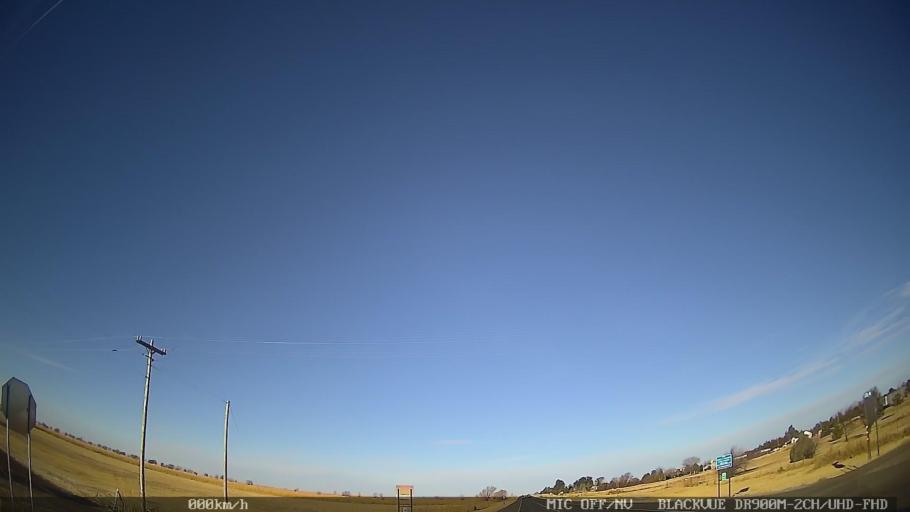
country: US
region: New Mexico
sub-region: Curry County
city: Clovis
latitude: 34.4340
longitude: -103.2491
